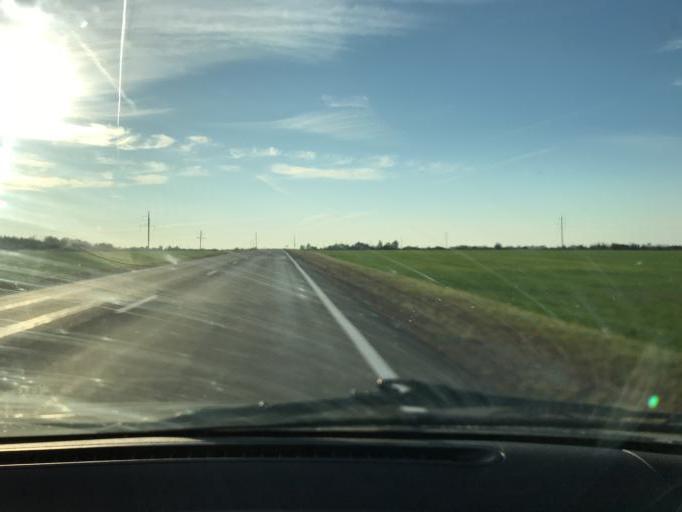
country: BY
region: Brest
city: Antopal'
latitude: 52.2197
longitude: 24.6848
